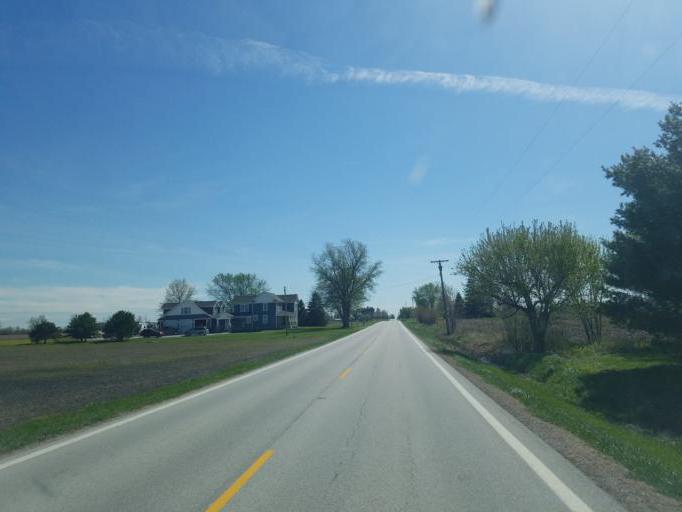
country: US
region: Ohio
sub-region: Huron County
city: Bellevue
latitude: 41.2298
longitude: -82.8109
